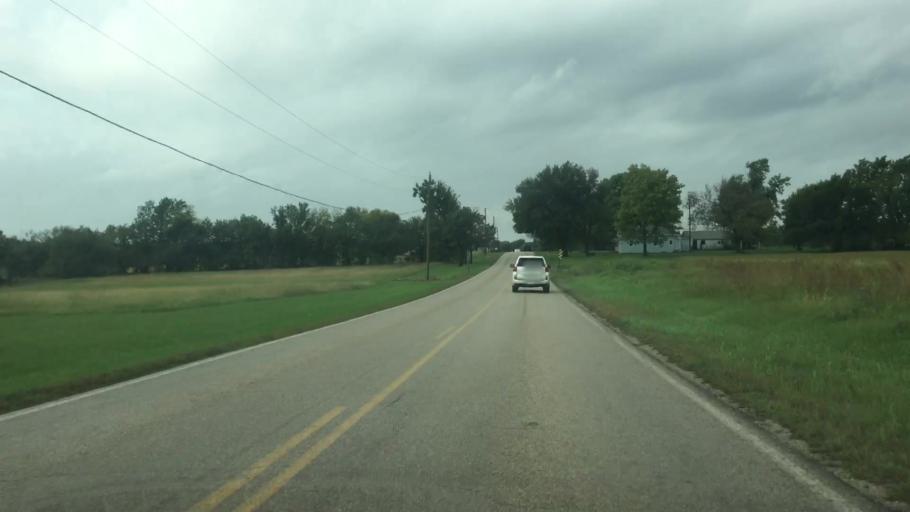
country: US
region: Kansas
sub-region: Allen County
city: Iola
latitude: 37.8857
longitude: -95.4216
